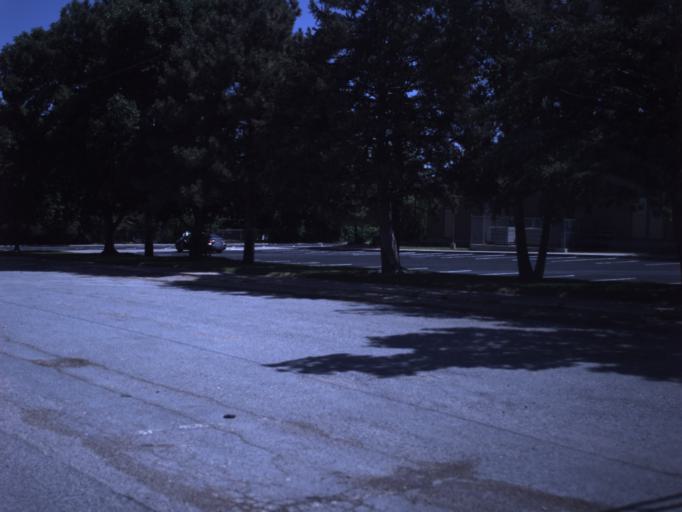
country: US
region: Utah
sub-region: Millard County
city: Delta
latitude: 39.3751
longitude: -112.3361
